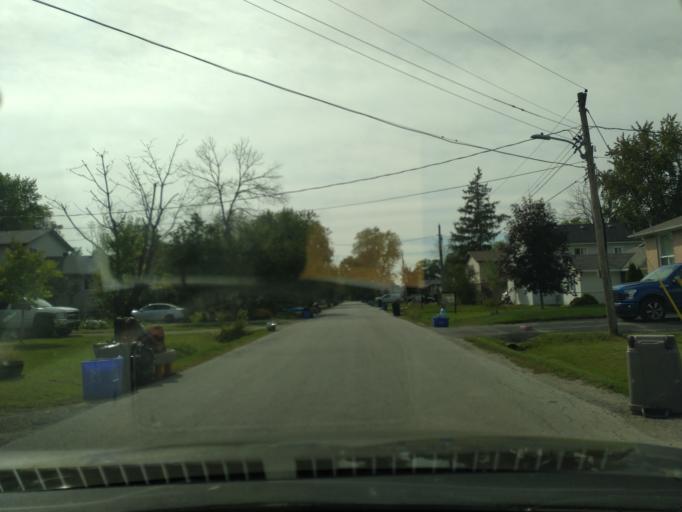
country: CA
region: Ontario
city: Keswick
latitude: 44.2159
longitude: -79.4695
